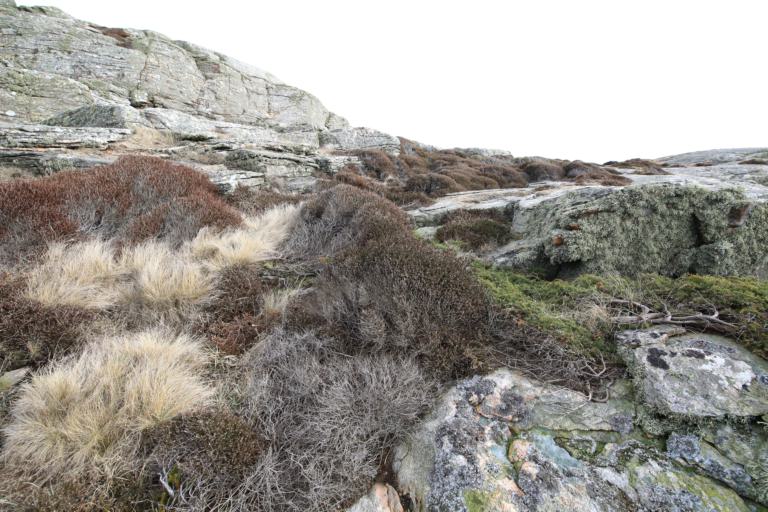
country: SE
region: Halland
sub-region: Kungsbacka Kommun
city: Frillesas
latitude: 57.2352
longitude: 12.0950
